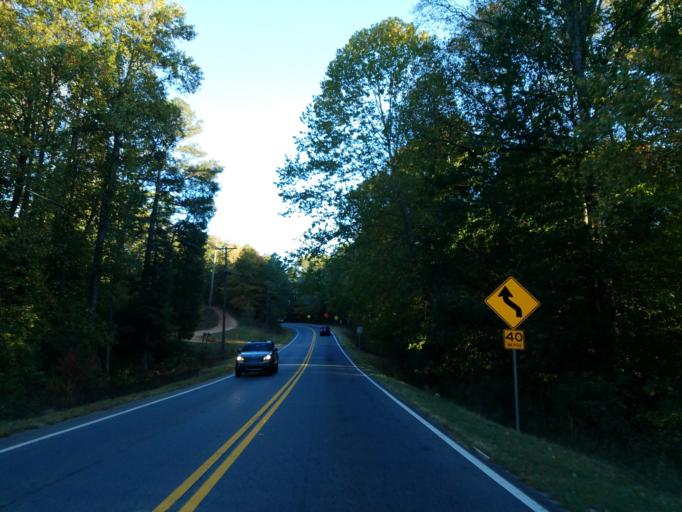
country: US
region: Georgia
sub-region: Dawson County
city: Dawsonville
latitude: 34.3755
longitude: -84.0461
